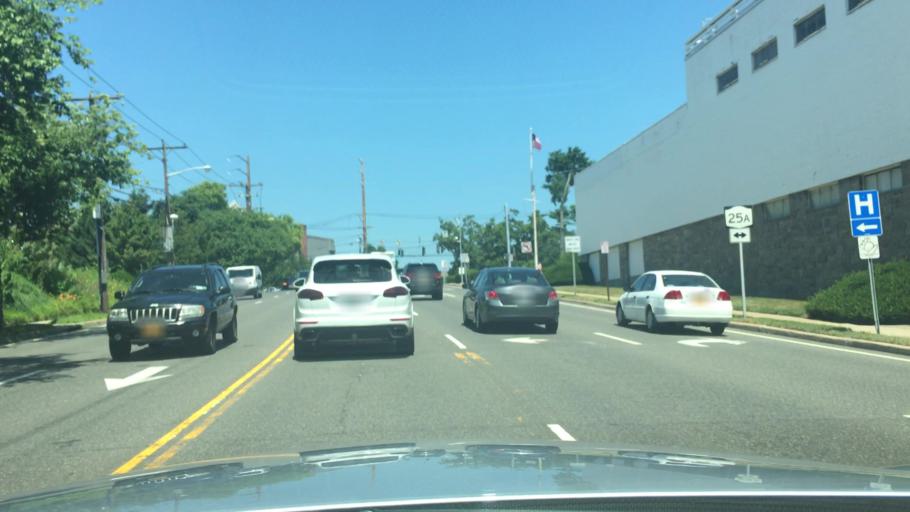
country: US
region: New York
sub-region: Nassau County
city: Manhasset
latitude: 40.7923
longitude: -73.6933
